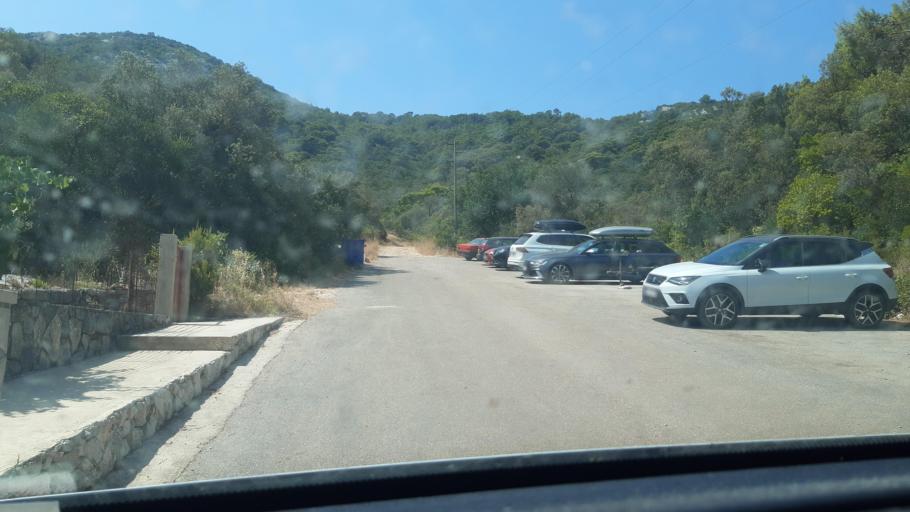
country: HR
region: Dubrovacko-Neretvanska
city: Ston
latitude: 42.7260
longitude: 17.6675
